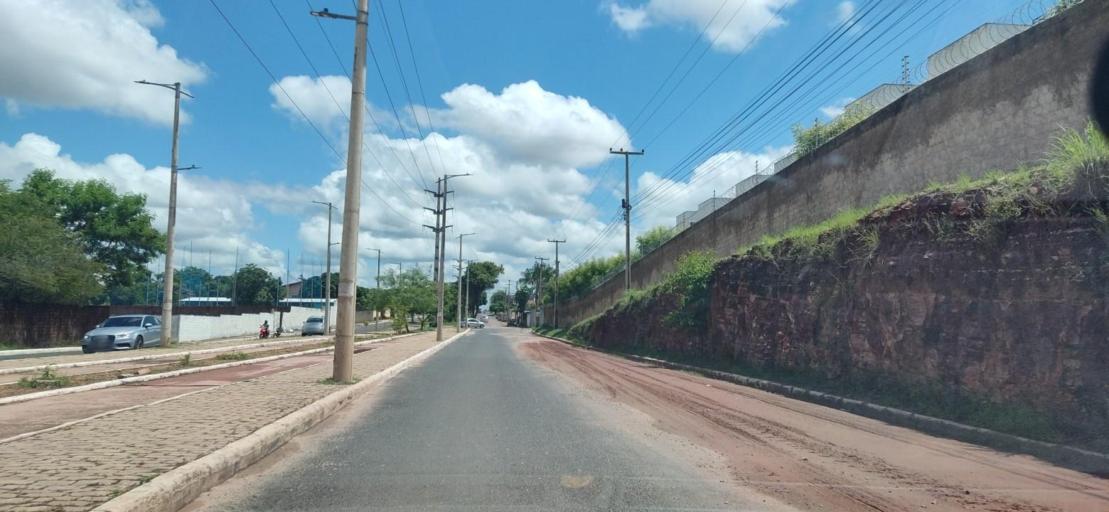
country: BR
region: Piaui
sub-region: Teresina
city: Teresina
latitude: -5.0739
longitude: -42.7514
